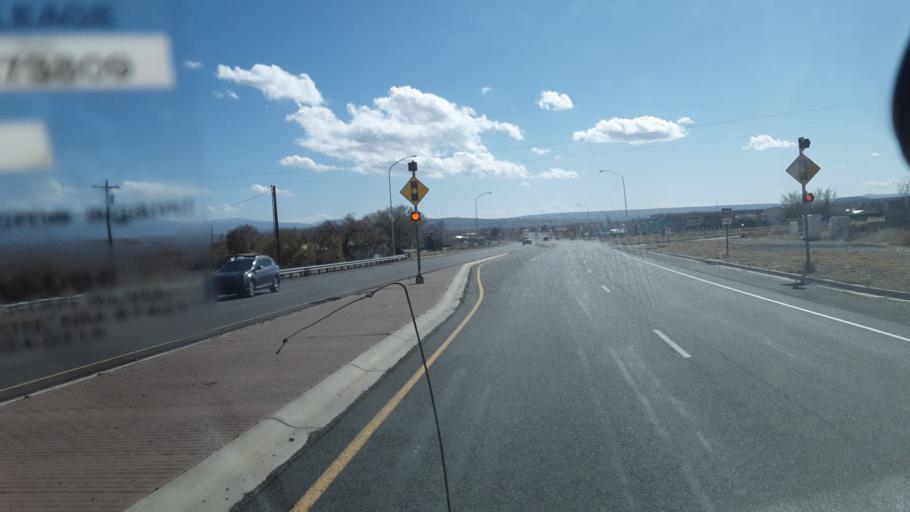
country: US
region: New Mexico
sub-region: Rio Arriba County
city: Espanola
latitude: 36.0114
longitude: -106.0887
